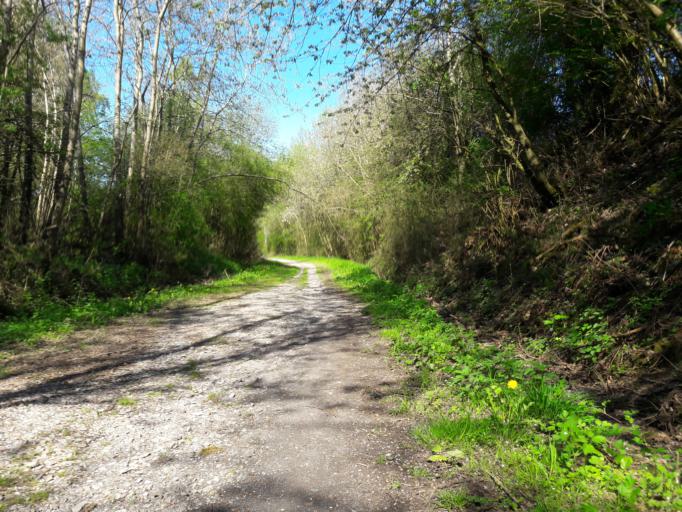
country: FR
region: Nord-Pas-de-Calais
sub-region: Departement du Nord
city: Sains-du-Nord
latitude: 50.1677
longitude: 4.0753
